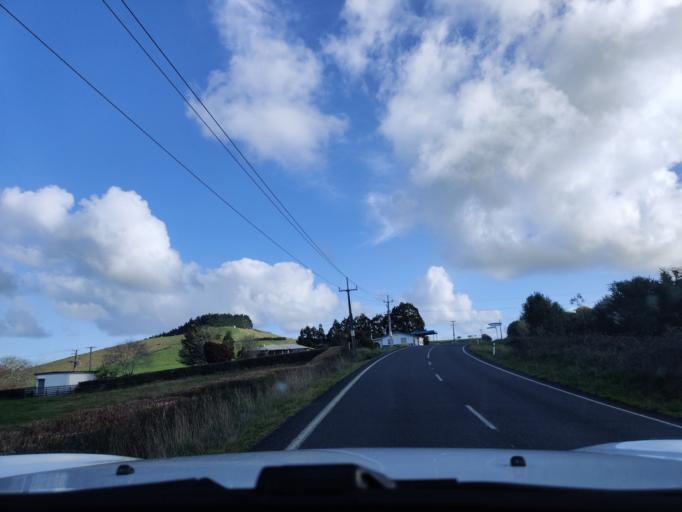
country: NZ
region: Waikato
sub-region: Waikato District
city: Te Kauwhata
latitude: -37.3678
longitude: 175.2456
